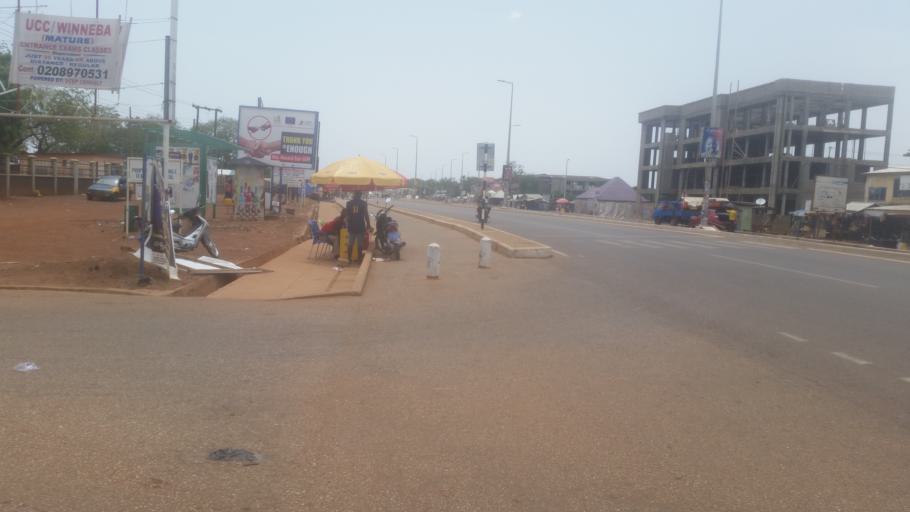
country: GH
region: Northern
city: Tamale
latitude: 9.3941
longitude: -0.8229
